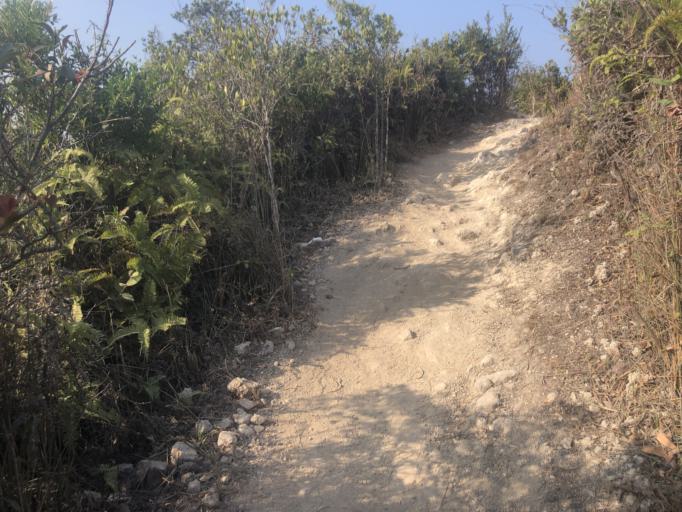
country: HK
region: Sai Kung
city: Sai Kung
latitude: 22.3604
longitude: 114.2946
